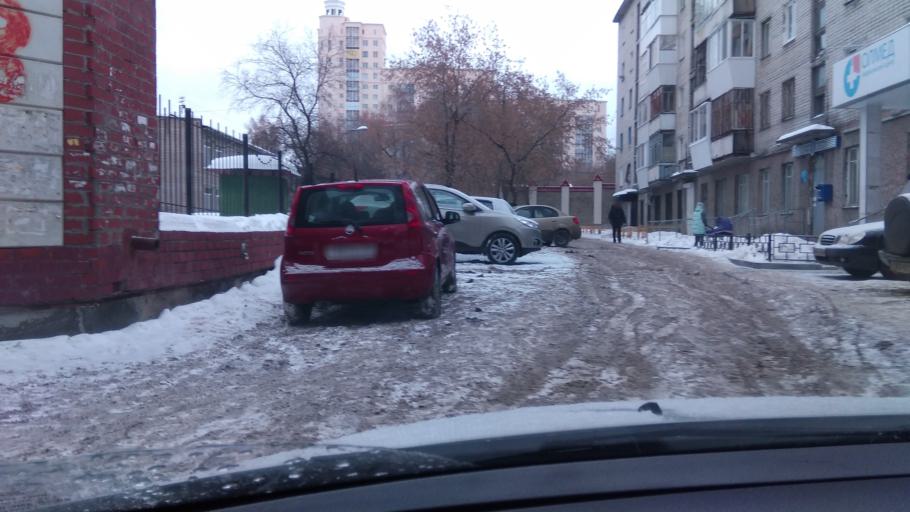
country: RU
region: Sverdlovsk
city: Yekaterinburg
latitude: 56.8158
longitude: 60.6170
